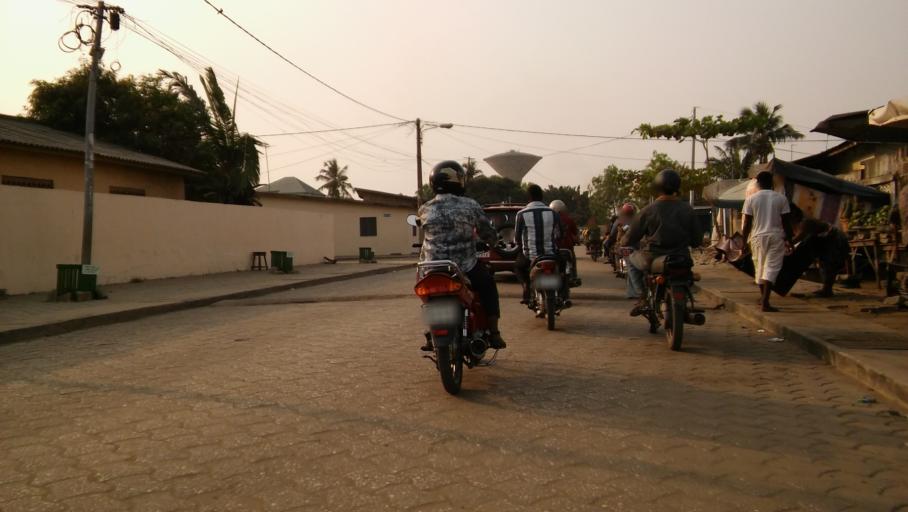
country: BJ
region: Littoral
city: Cotonou
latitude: 6.3810
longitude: 2.3884
